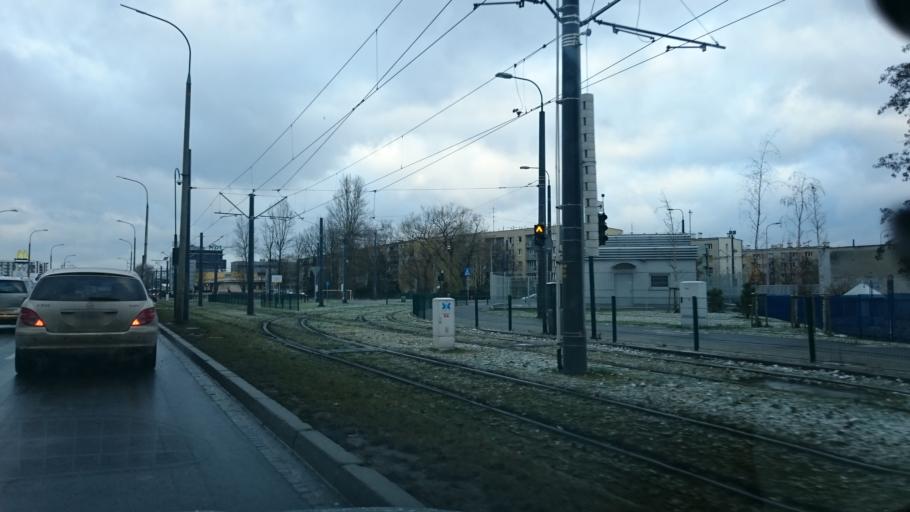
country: PL
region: Lesser Poland Voivodeship
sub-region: Krakow
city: Krakow
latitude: 50.0306
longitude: 19.9730
